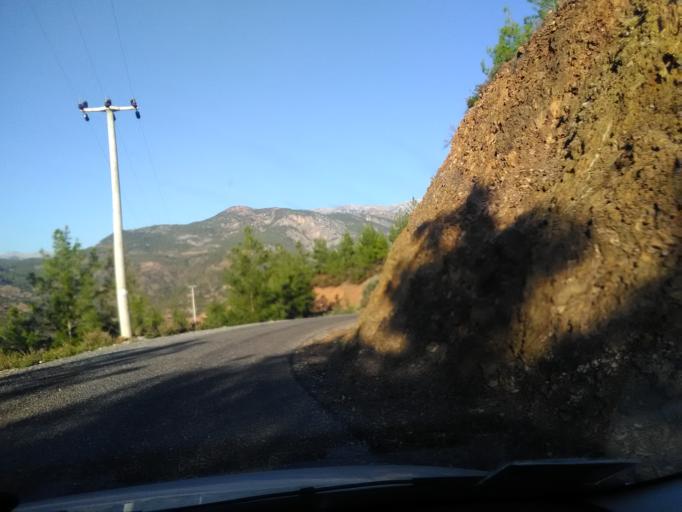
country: TR
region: Antalya
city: Gazipasa
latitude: 36.3062
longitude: 32.4028
